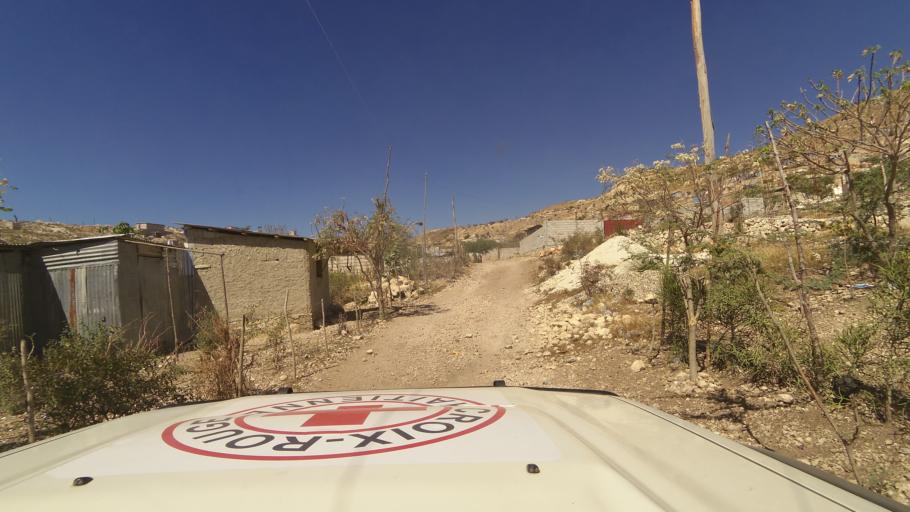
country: HT
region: Ouest
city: Croix des Bouquets
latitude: 18.6629
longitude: -72.2683
